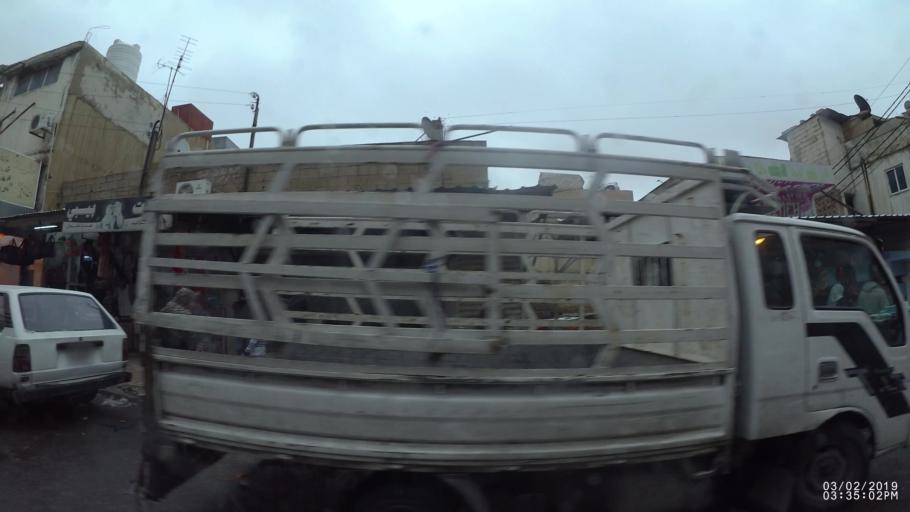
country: JO
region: Amman
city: Amman
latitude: 31.9687
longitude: 35.9256
